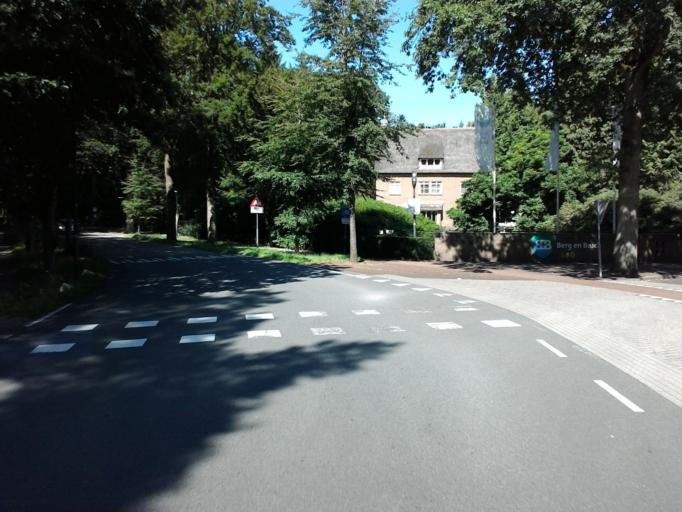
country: NL
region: Utrecht
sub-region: Gemeente De Bilt
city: De Bilt
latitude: 52.1546
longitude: 5.2035
